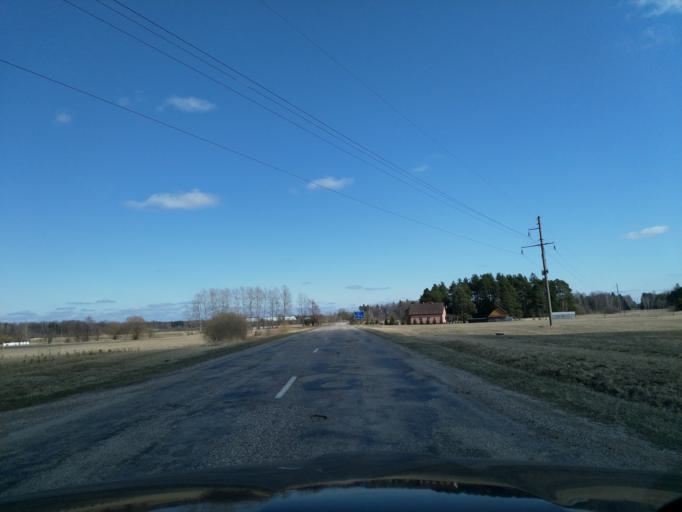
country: LV
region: Kuldigas Rajons
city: Kuldiga
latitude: 56.9722
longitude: 22.0050
